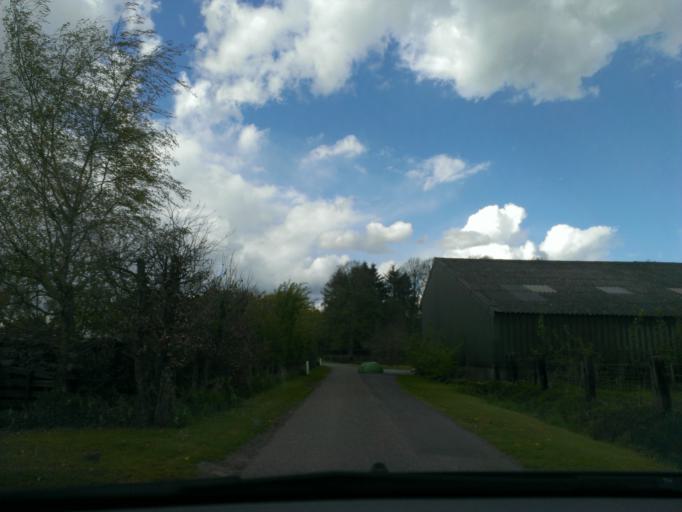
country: NL
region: Gelderland
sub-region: Gemeente Voorst
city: Twello
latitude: 52.2353
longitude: 6.0526
